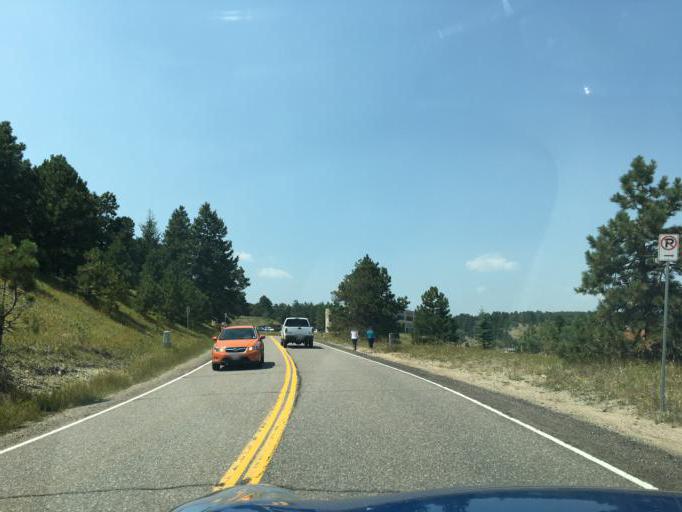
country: US
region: Colorado
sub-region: Jefferson County
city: Genesee
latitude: 39.7065
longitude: -105.2817
